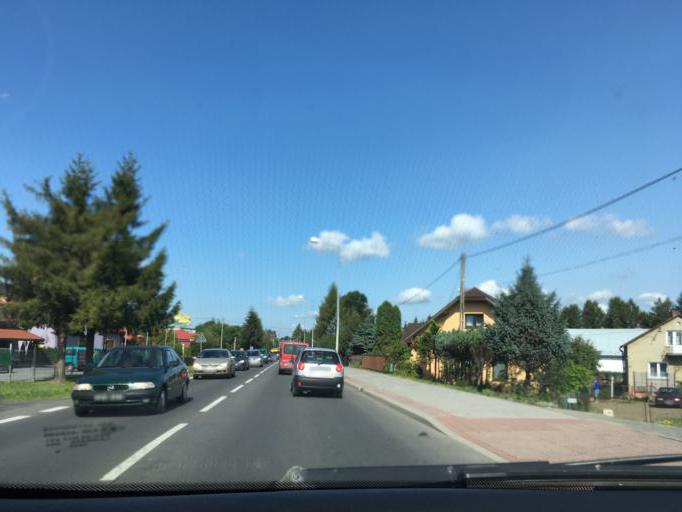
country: PL
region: Subcarpathian Voivodeship
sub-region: Powiat sanocki
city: Zagorz
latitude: 49.5175
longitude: 22.2625
